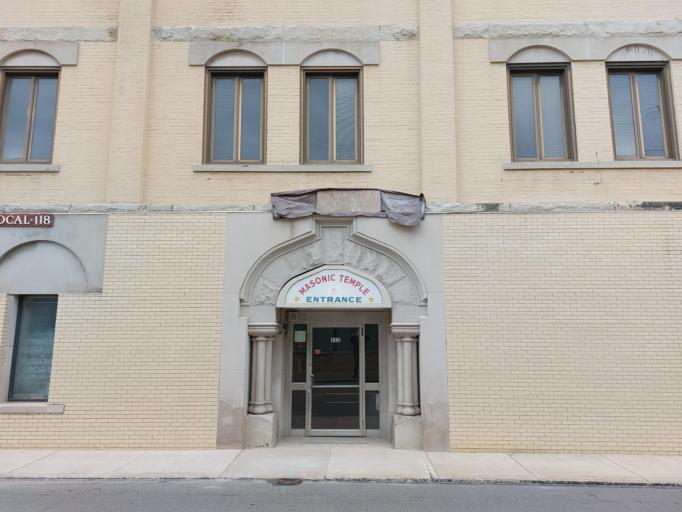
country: US
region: Ohio
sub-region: Trumbull County
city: Warren
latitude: 41.2363
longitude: -80.8161
